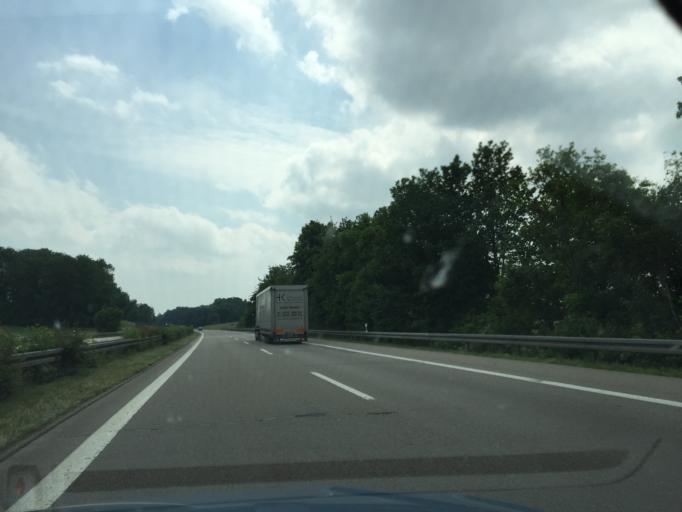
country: DE
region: Bavaria
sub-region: Swabia
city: Holzheim
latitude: 48.3938
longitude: 10.0880
